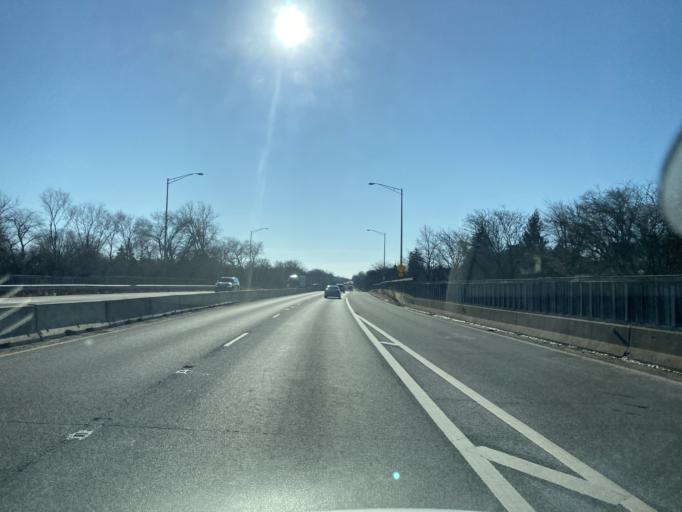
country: US
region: Illinois
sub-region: DuPage County
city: Hinsdale
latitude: 41.8100
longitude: -87.9468
